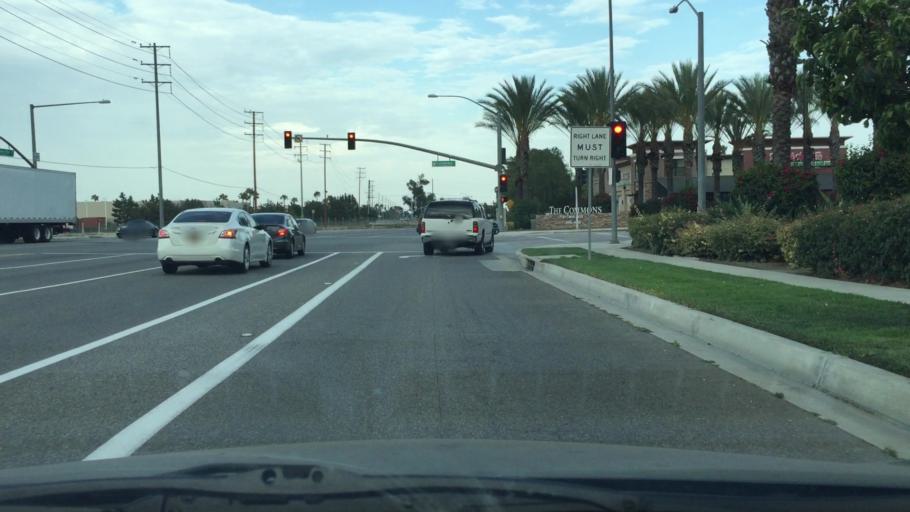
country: US
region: California
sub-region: San Bernardino County
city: Los Serranos
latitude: 33.9825
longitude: -117.7026
